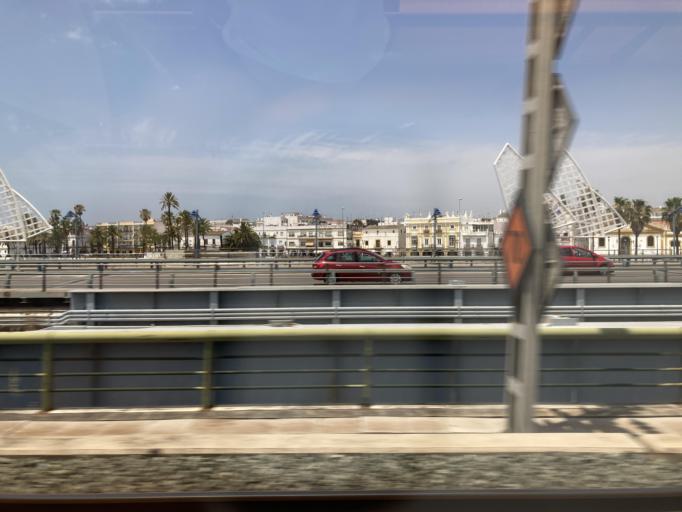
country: ES
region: Andalusia
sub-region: Provincia de Cadiz
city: El Puerto de Santa Maria
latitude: 36.6007
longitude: -6.2198
